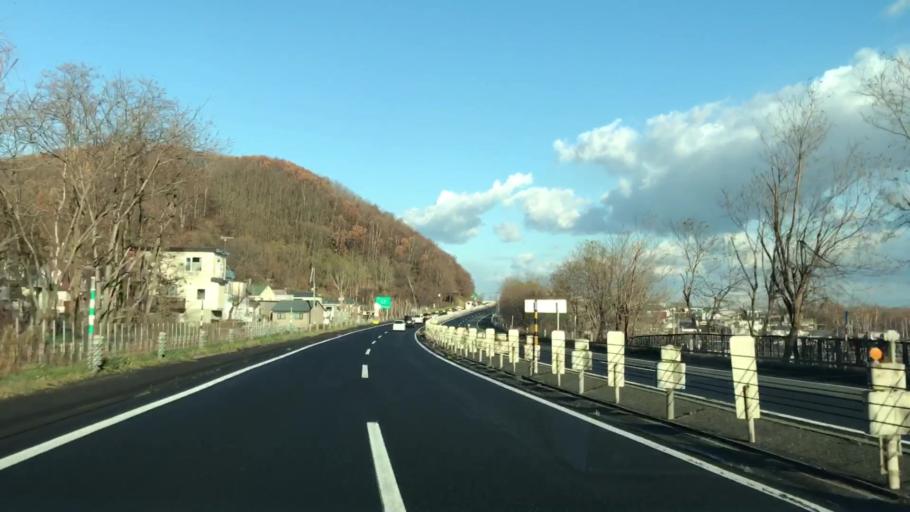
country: JP
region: Hokkaido
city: Sapporo
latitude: 43.1041
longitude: 141.2440
